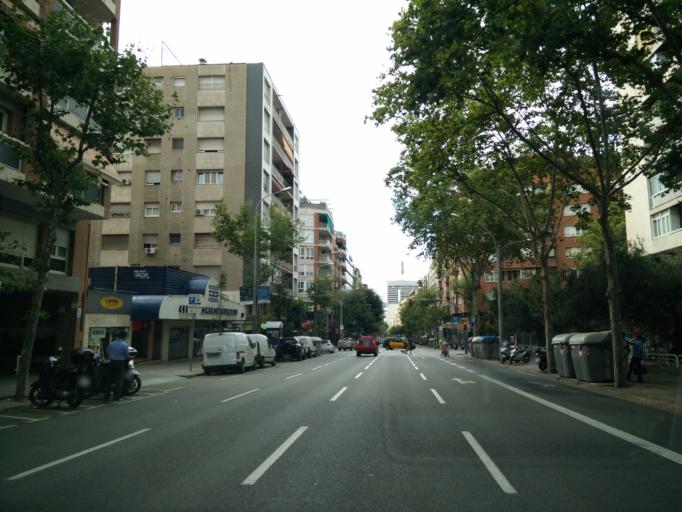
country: ES
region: Catalonia
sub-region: Provincia de Barcelona
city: les Corts
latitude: 41.3856
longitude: 2.1366
